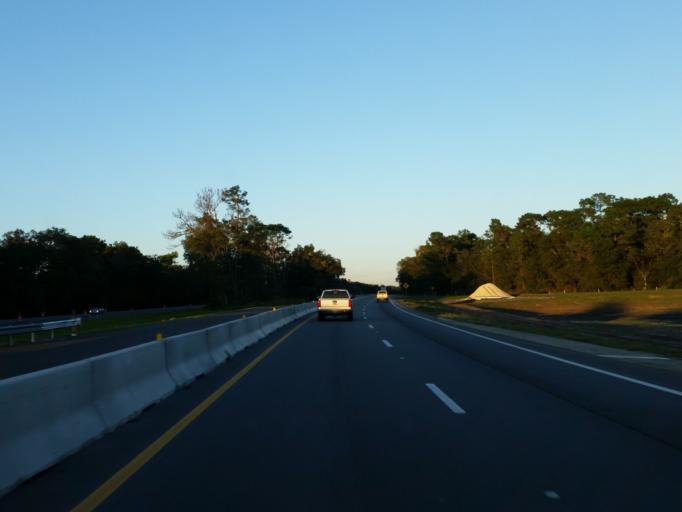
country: US
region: Florida
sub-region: Hernando County
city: Ridge Manor
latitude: 28.6043
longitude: -82.2018
